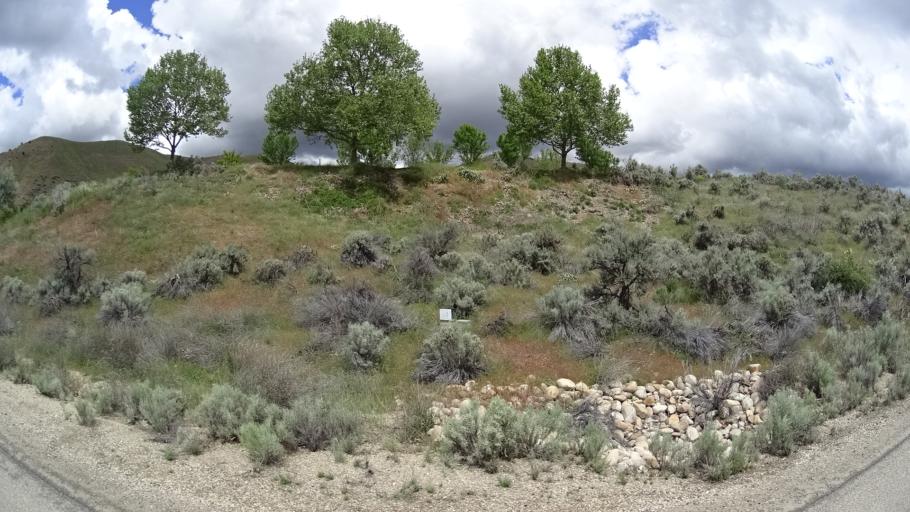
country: US
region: Idaho
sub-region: Ada County
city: Garden City
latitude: 43.6642
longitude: -116.2197
